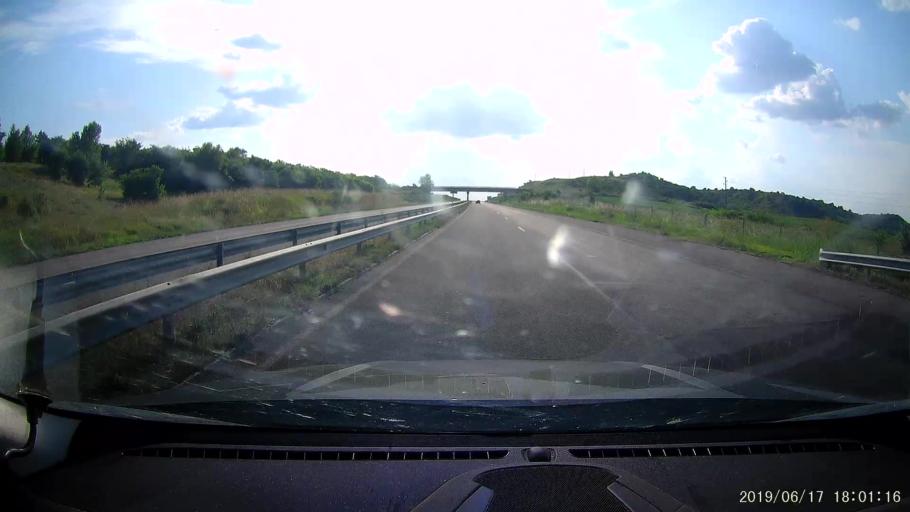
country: BG
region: Khaskovo
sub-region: Obshtina Svilengrad
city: Svilengrad
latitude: 41.7450
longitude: 26.2598
